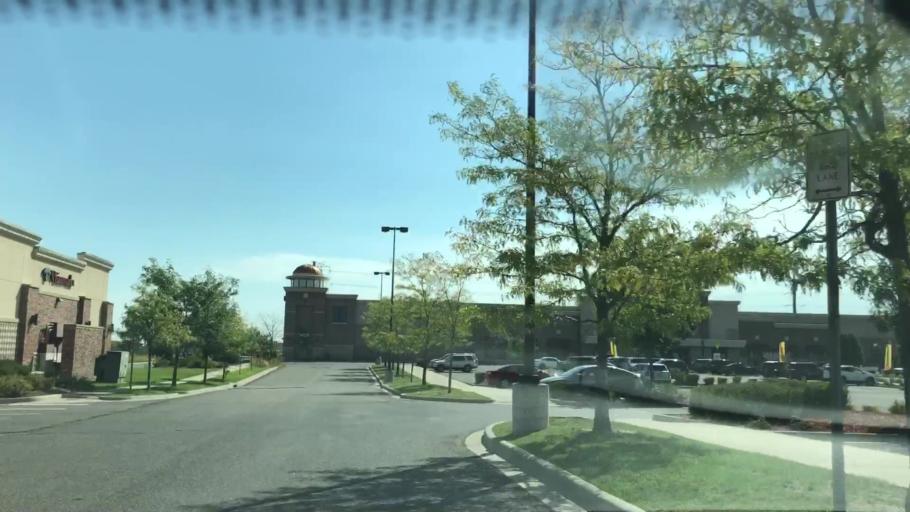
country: US
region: Colorado
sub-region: Douglas County
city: Parker
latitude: 39.6022
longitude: -104.7067
